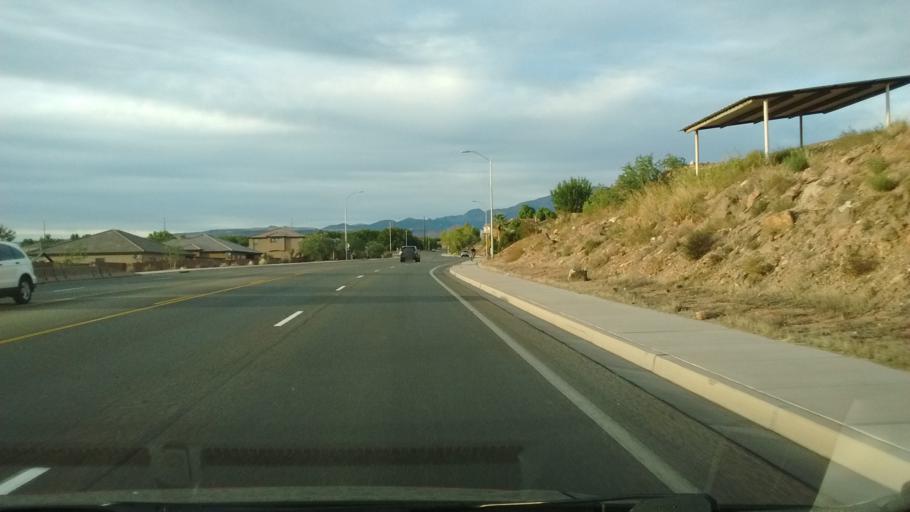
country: US
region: Utah
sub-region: Washington County
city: Washington
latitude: 37.1207
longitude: -113.5046
